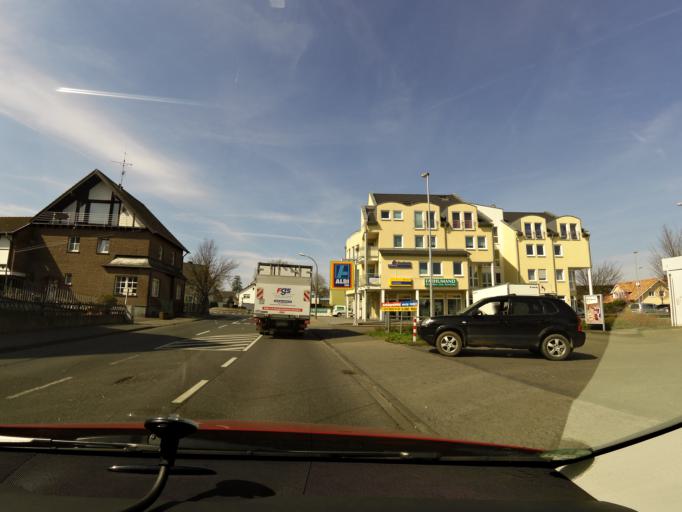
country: DE
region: North Rhine-Westphalia
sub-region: Regierungsbezirk Koln
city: Rheinbach
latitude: 50.6251
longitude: 6.9597
